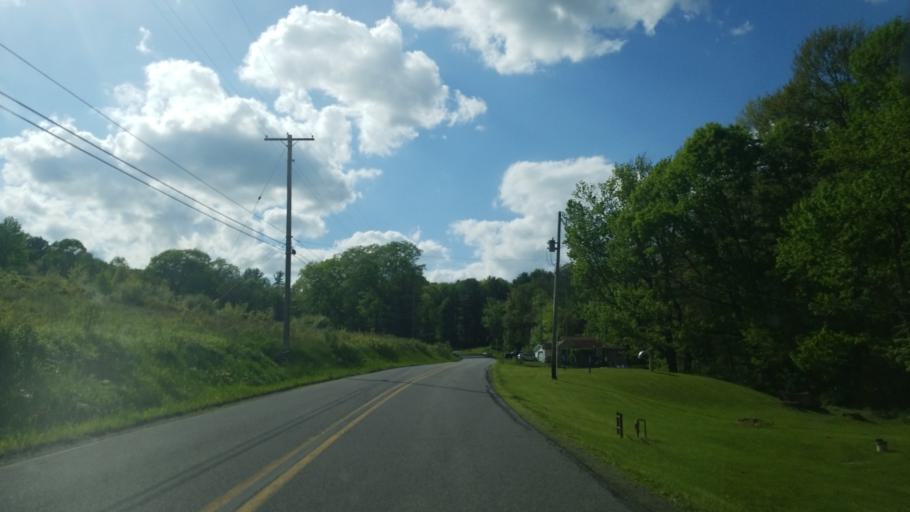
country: US
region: Pennsylvania
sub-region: Clearfield County
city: Troy
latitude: 40.9325
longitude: -78.3022
